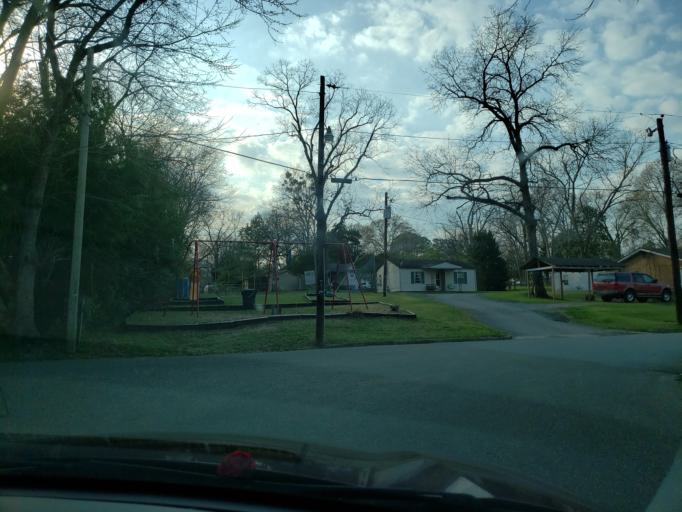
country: US
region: Alabama
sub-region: Hale County
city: Greensboro
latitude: 32.7053
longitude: -87.5990
